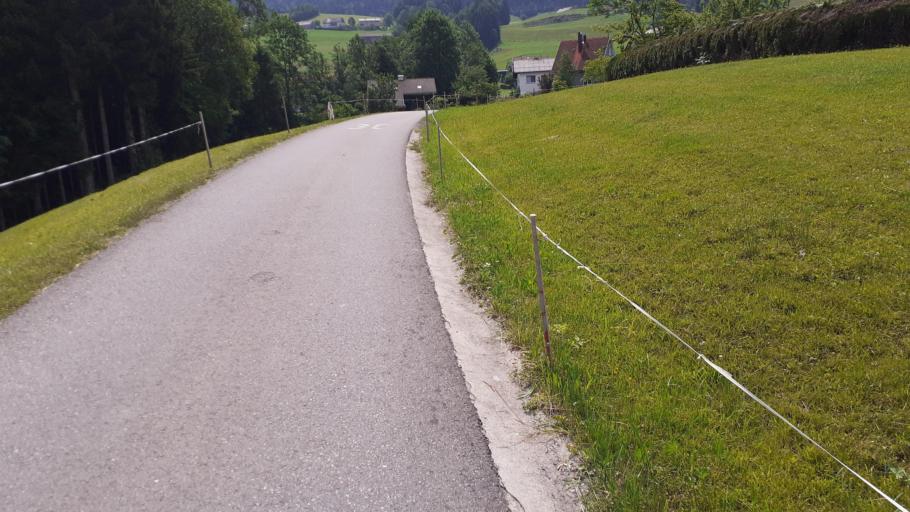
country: AT
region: Vorarlberg
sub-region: Politischer Bezirk Bregenz
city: Bildstein
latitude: 47.4476
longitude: 9.8164
